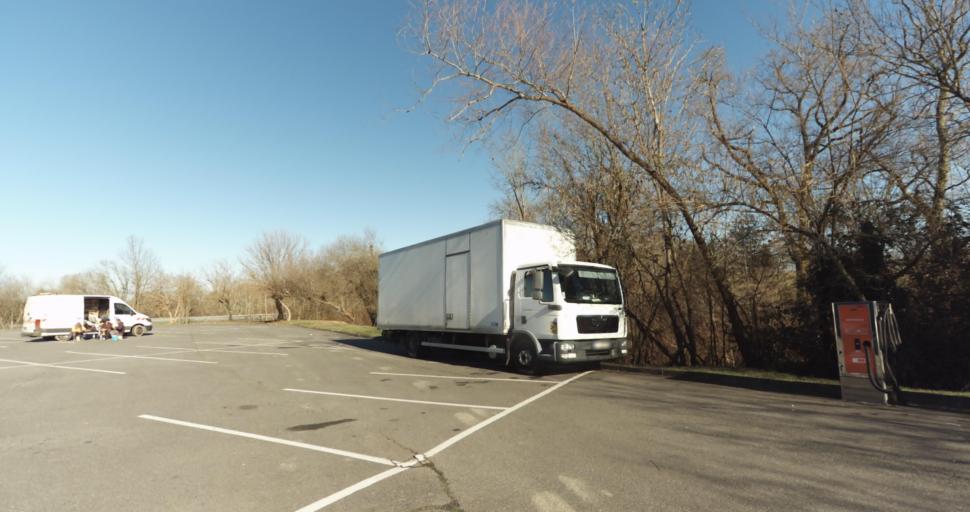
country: FR
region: Aquitaine
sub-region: Departement des Pyrenees-Atlantiques
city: Morlaas
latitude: 43.3508
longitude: -0.2621
